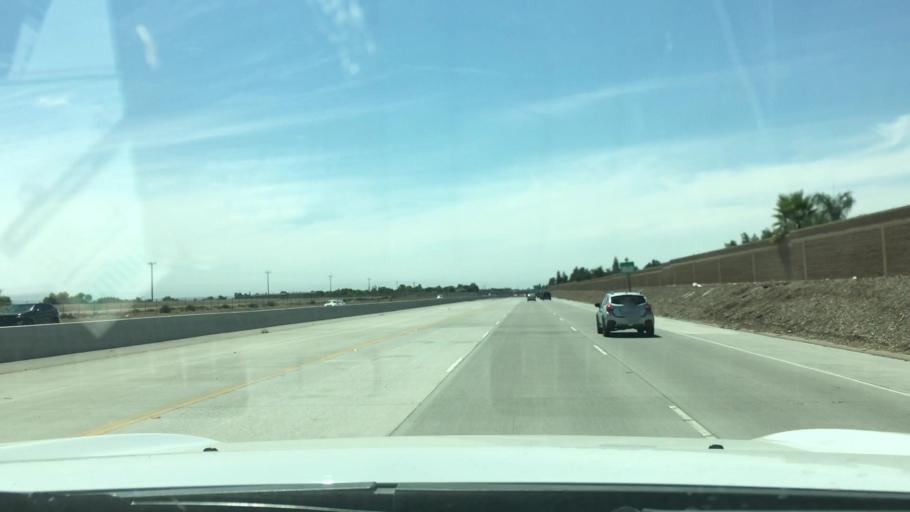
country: US
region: California
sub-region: Kern County
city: Greenacres
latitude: 35.3620
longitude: -119.1016
